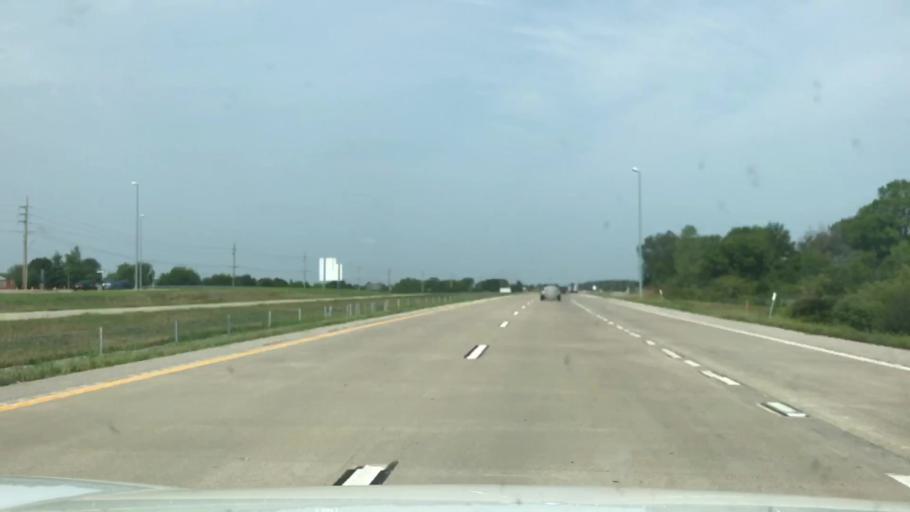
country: US
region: Missouri
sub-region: Saint Charles County
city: Dardenne Prairie
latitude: 38.7552
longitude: -90.7049
